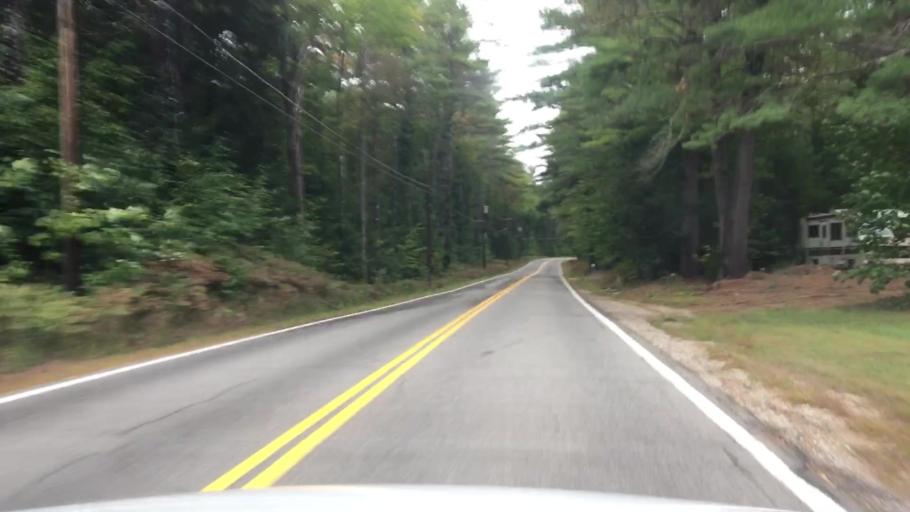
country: US
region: New Hampshire
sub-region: Carroll County
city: Effingham
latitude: 43.7243
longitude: -71.0004
